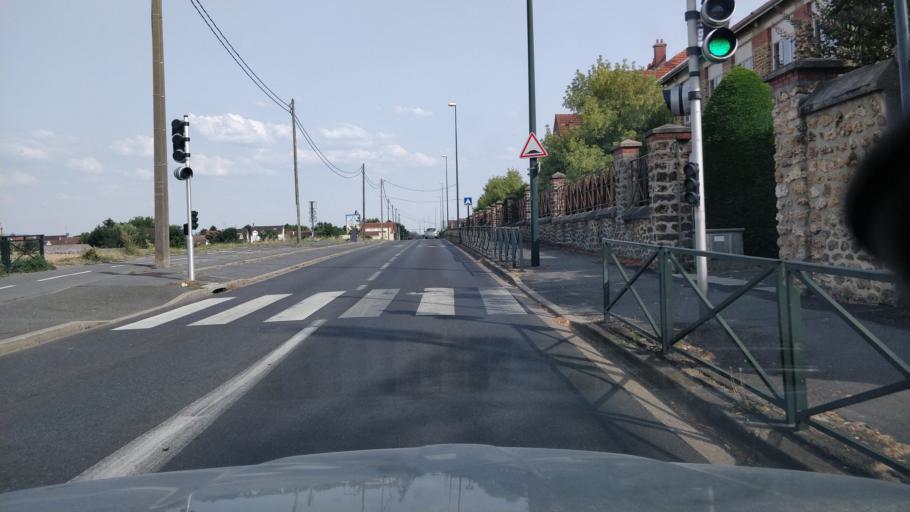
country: FR
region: Ile-de-France
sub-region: Departement de Seine-et-Marne
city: Brou-sur-Chantereine
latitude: 48.8880
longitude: 2.6147
